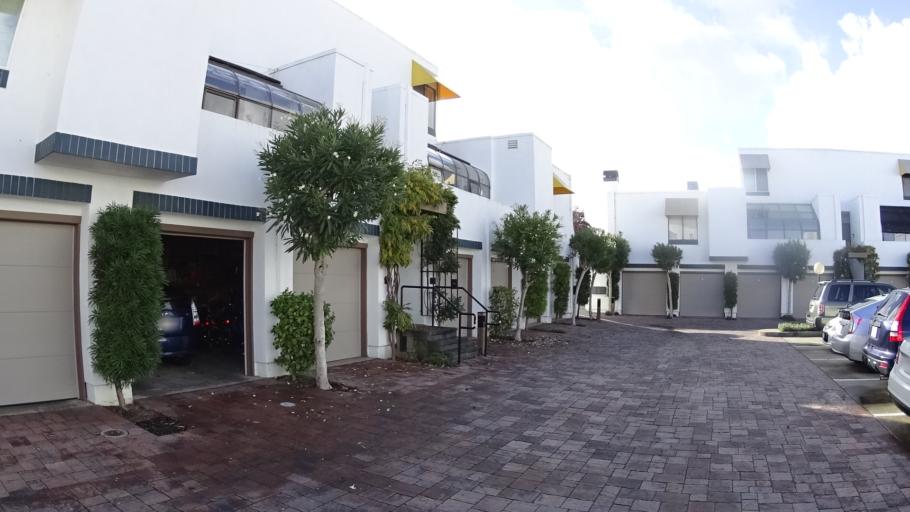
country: US
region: California
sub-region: San Mateo County
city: Foster City
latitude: 37.5541
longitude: -122.2692
